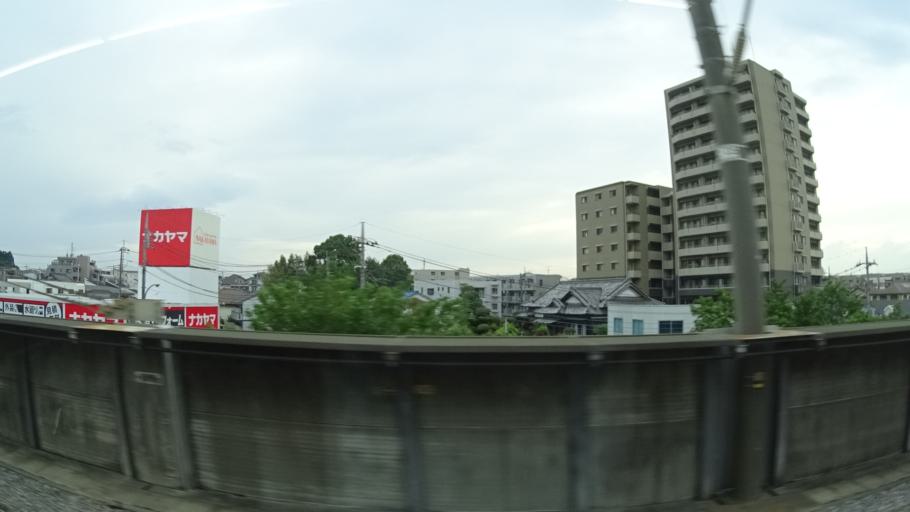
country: JP
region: Saitama
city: Yono
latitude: 35.8617
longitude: 139.6331
